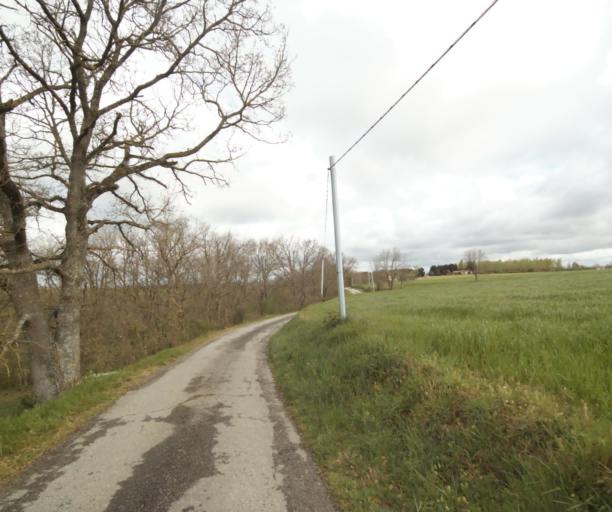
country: FR
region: Midi-Pyrenees
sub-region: Departement de l'Ariege
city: Saverdun
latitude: 43.2206
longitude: 1.5591
